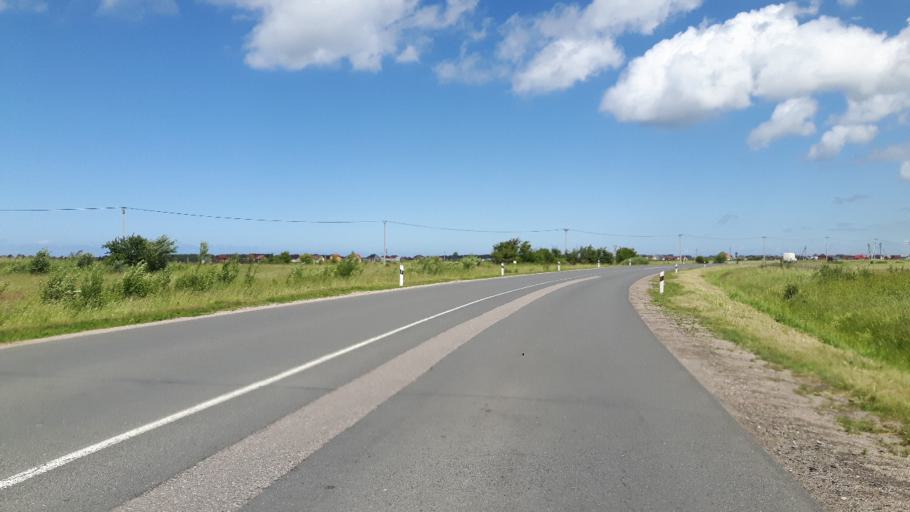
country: RU
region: Kaliningrad
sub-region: Zelenogradskiy Rayon
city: Zelenogradsk
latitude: 54.9275
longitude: 20.3992
